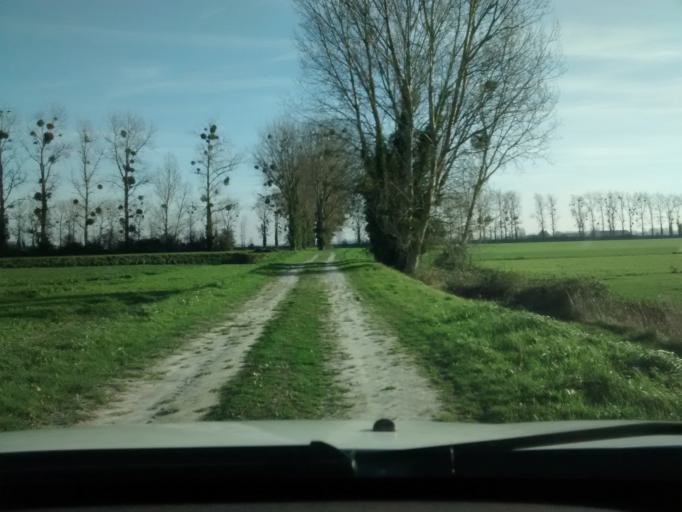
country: FR
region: Brittany
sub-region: Departement d'Ille-et-Vilaine
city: Roz-sur-Couesnon
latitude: 48.6111
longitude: -1.5986
